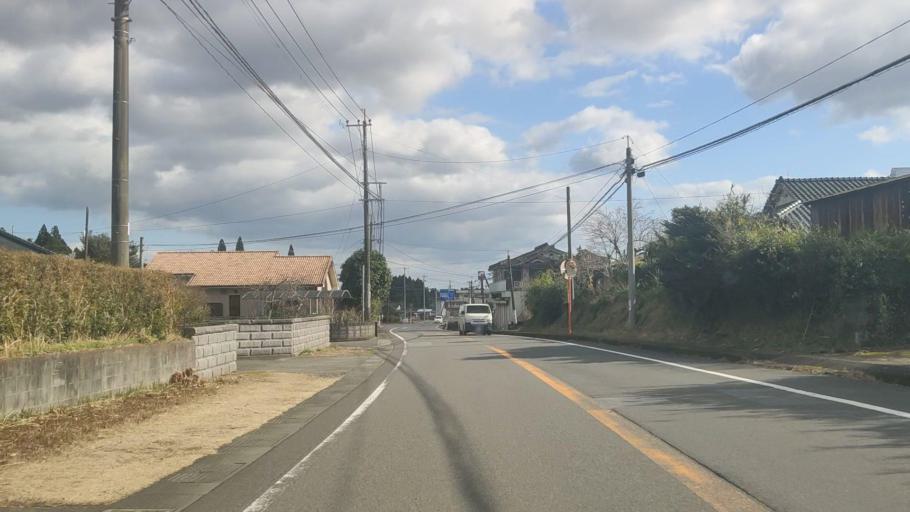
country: JP
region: Kagoshima
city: Kajiki
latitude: 31.8201
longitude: 130.7012
